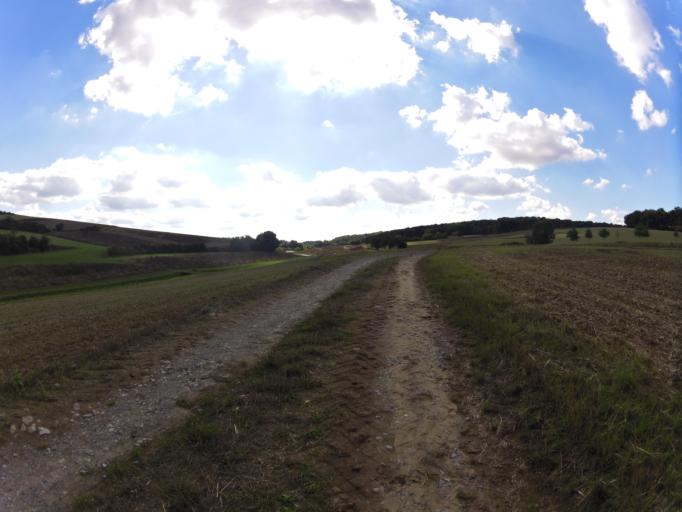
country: DE
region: Bavaria
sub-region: Regierungsbezirk Unterfranken
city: Frickenhausen
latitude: 49.6936
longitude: 10.0846
